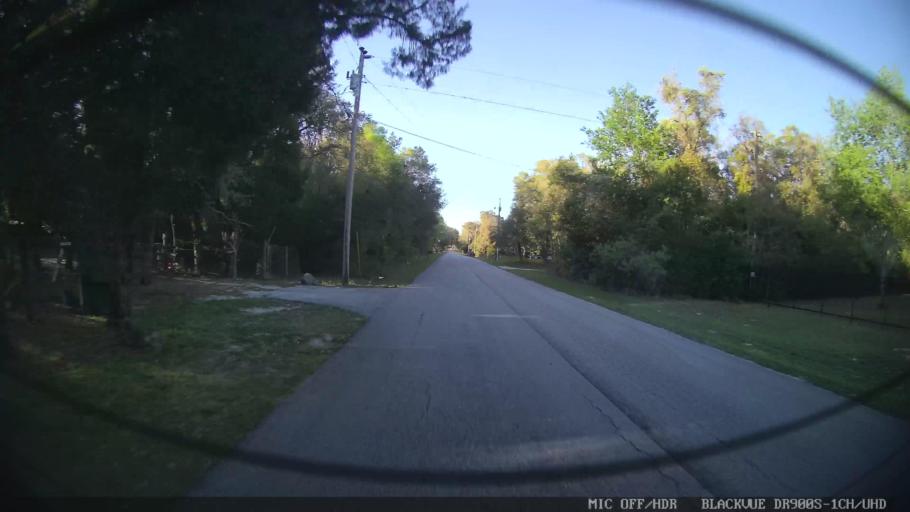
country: US
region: Florida
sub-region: Pasco County
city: Shady Hills
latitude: 28.4046
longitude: -82.5737
